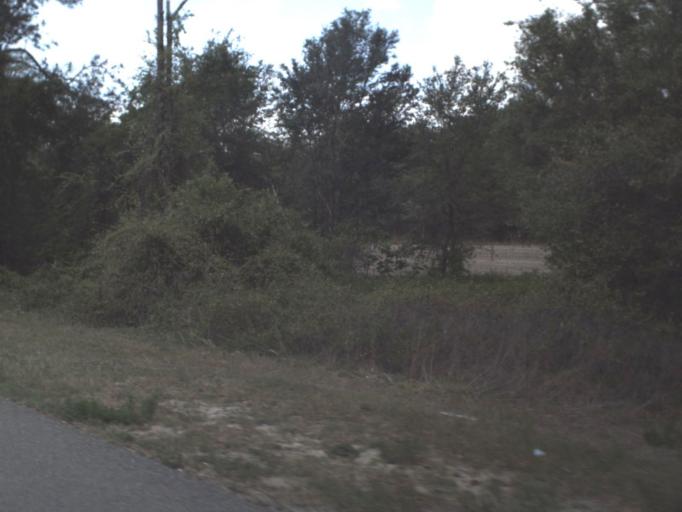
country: US
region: Florida
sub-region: Citrus County
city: Hernando
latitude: 29.0331
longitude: -82.3043
